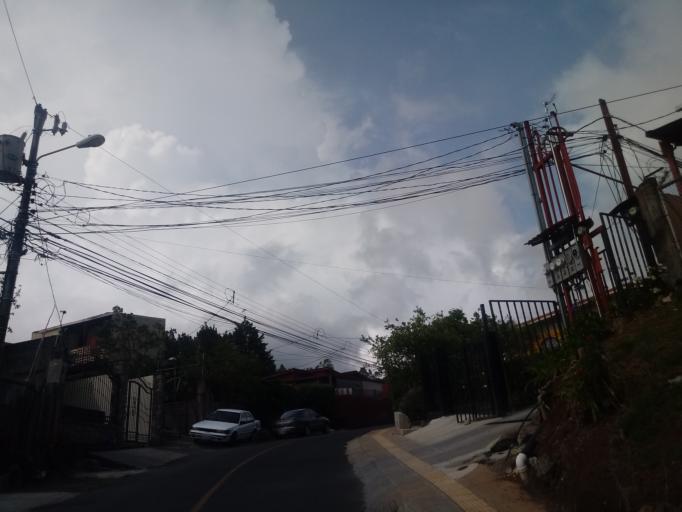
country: CR
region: Heredia
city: Angeles
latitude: 10.0266
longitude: -84.0470
